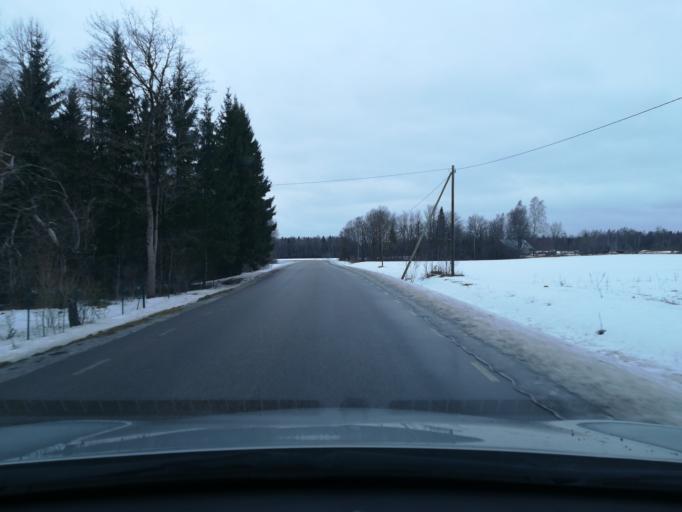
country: EE
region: Harju
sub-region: Nissi vald
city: Riisipere
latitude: 59.1312
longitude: 24.3018
